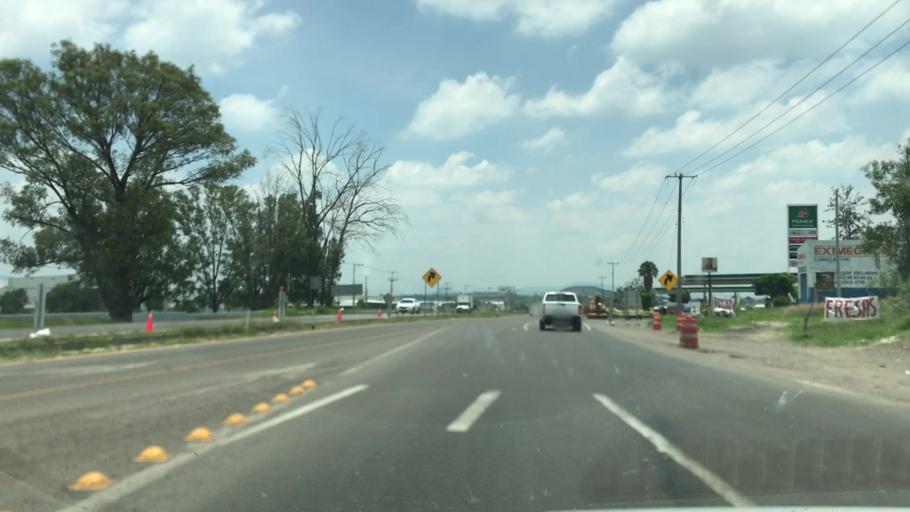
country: MX
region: Guanajuato
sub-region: Irapuato
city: San Ignacio de Rivera (Ojo de Agua)
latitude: 20.5640
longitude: -101.4477
